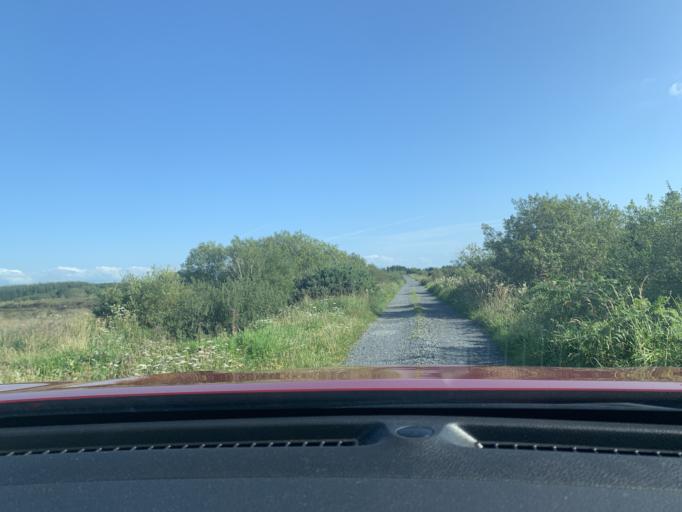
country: IE
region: Connaught
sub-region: Sligo
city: Tobercurry
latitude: 54.0691
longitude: -8.7956
